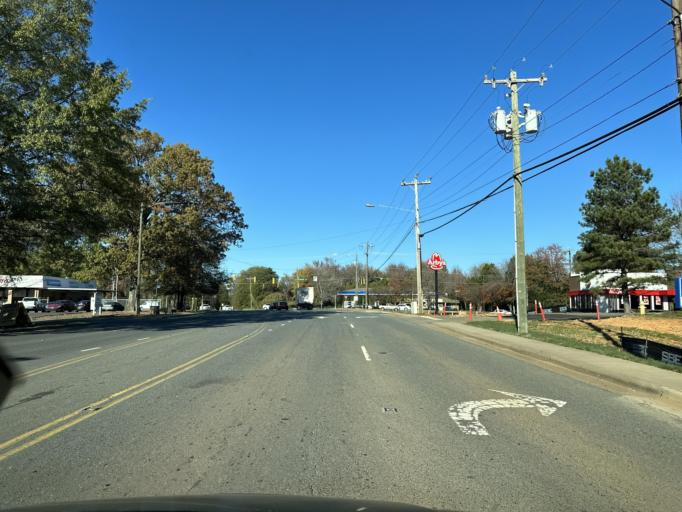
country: US
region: North Carolina
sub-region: Gaston County
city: Mount Holly
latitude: 35.2448
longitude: -80.9372
